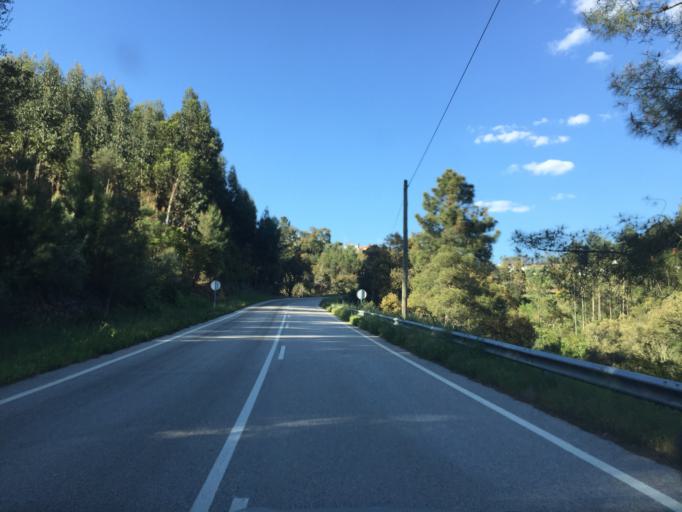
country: PT
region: Leiria
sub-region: Pedrogao Grande
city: Pedrogao Grande
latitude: 39.9852
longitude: -8.0747
